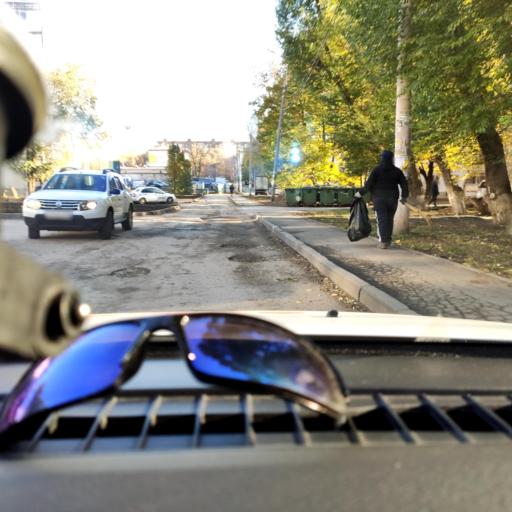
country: RU
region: Samara
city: Samara
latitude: 53.2384
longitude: 50.2286
